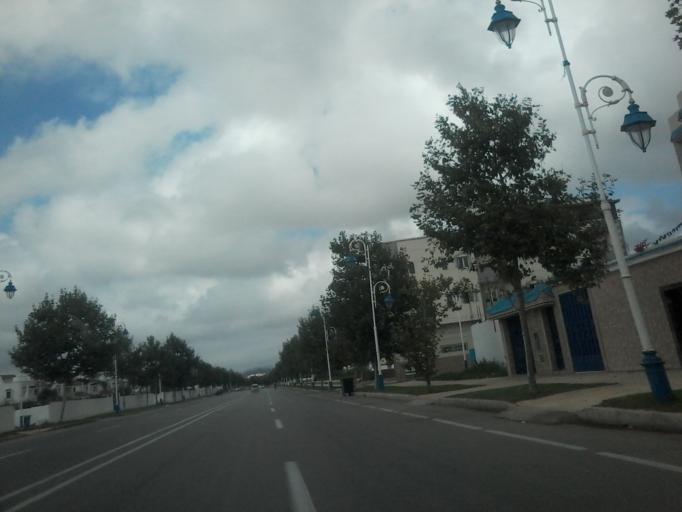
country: MA
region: Tanger-Tetouan
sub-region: Tetouan
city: Martil
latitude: 35.6381
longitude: -5.2901
